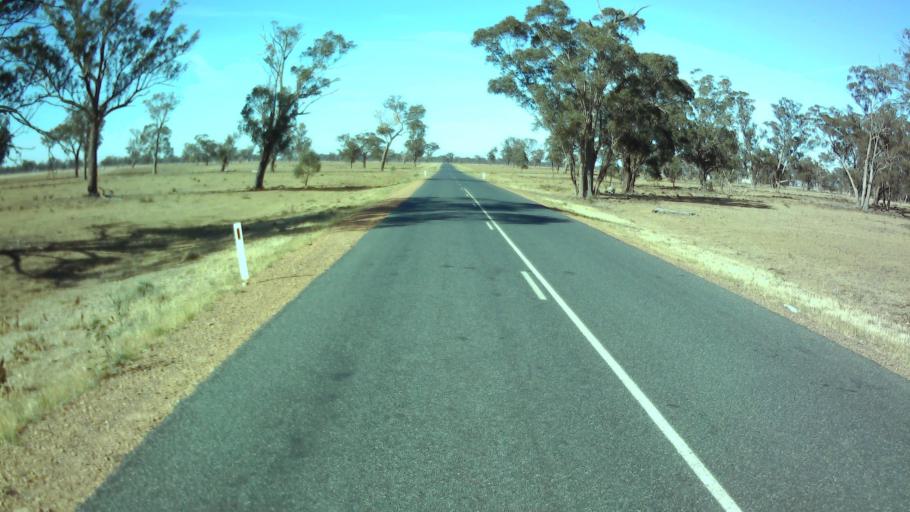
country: AU
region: New South Wales
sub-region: Weddin
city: Grenfell
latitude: -34.0432
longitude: 147.9278
